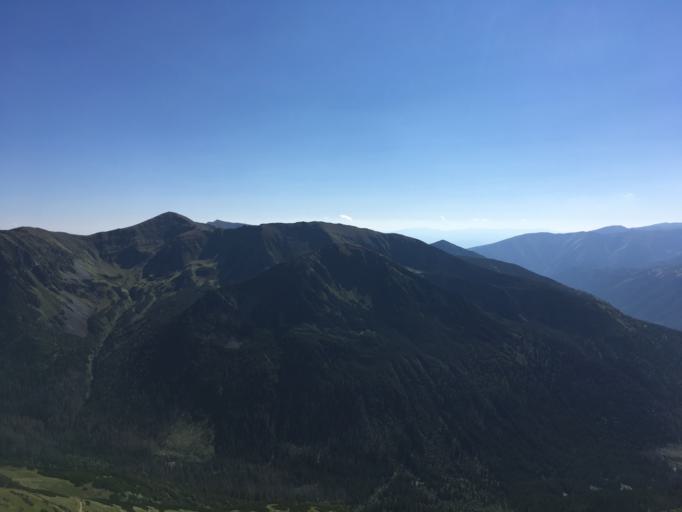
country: PL
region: Lesser Poland Voivodeship
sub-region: Powiat tatrzanski
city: Zakopane
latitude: 49.2302
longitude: 19.9844
